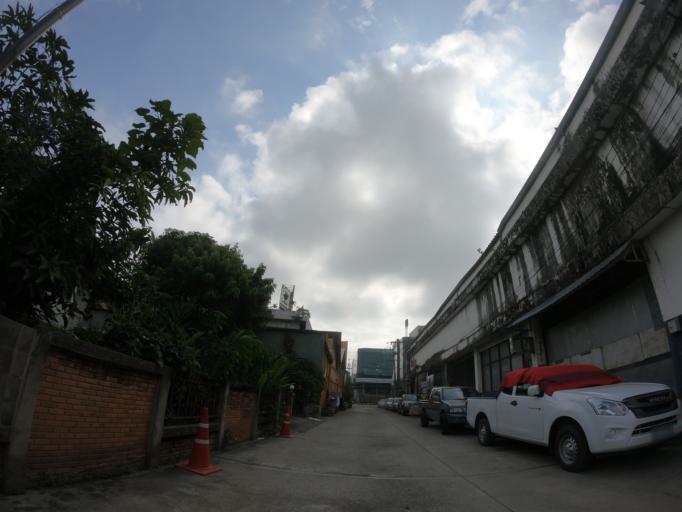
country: TH
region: Chiang Mai
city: Chiang Mai
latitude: 18.7627
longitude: 98.9722
